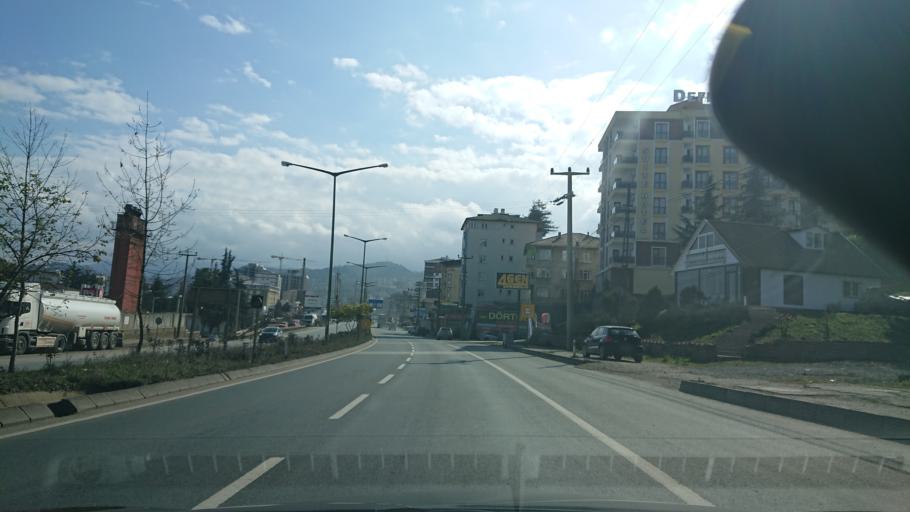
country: TR
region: Trabzon
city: Yomra
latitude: 40.9734
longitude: 39.8320
